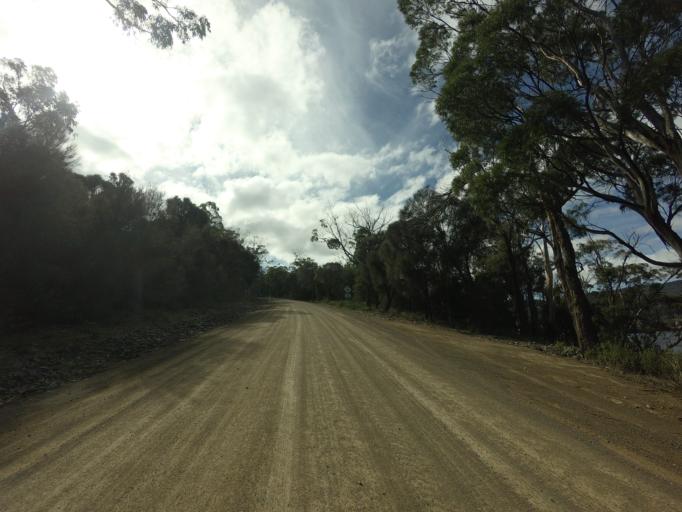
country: AU
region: Tasmania
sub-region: Clarence
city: Sandford
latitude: -43.0963
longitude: 147.7212
